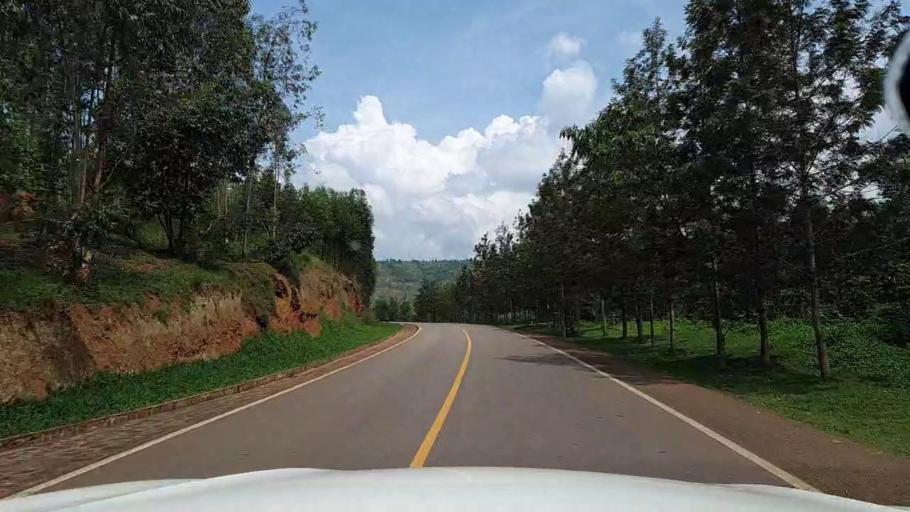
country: RW
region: Kigali
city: Kigali
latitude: -1.8542
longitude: 30.0973
